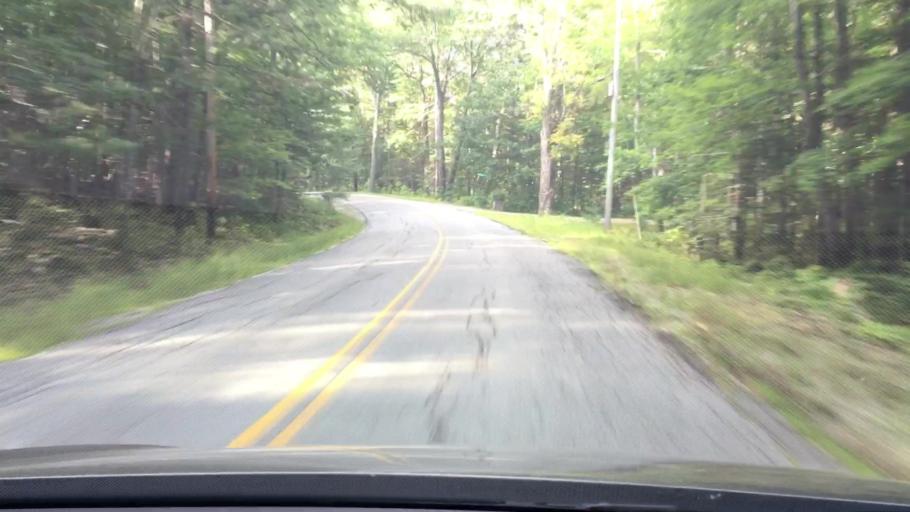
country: US
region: Maine
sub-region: Hancock County
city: Orland
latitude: 44.5301
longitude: -68.7635
